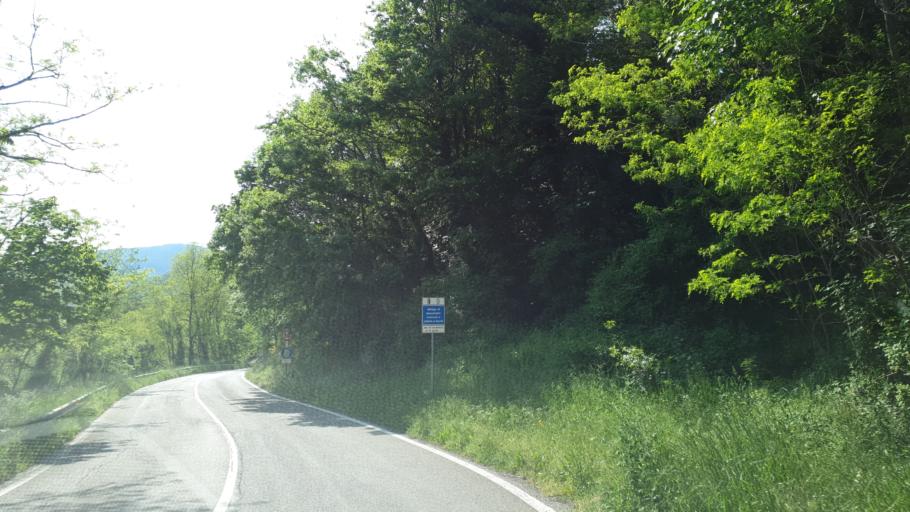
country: IT
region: Tuscany
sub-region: Province of Arezzo
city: Soci
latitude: 43.7716
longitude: 11.8594
